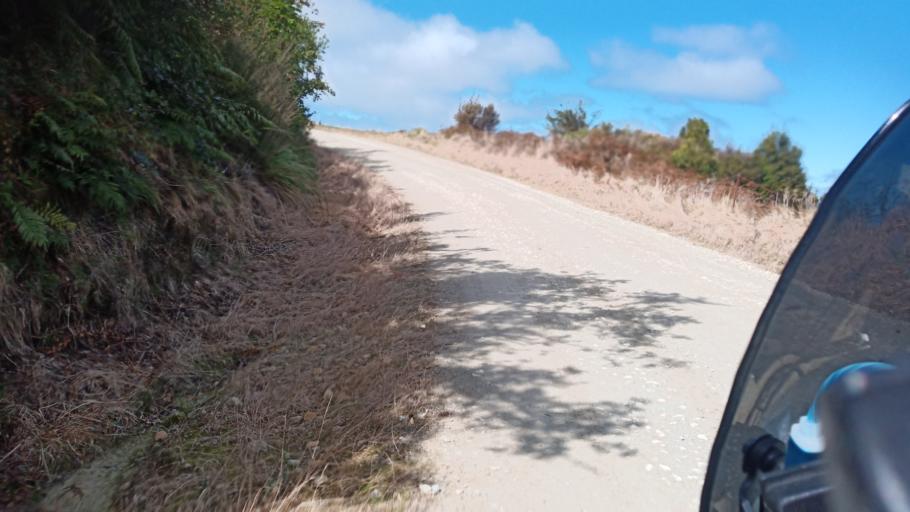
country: NZ
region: Gisborne
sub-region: Gisborne District
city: Gisborne
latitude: -38.8548
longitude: 177.7915
